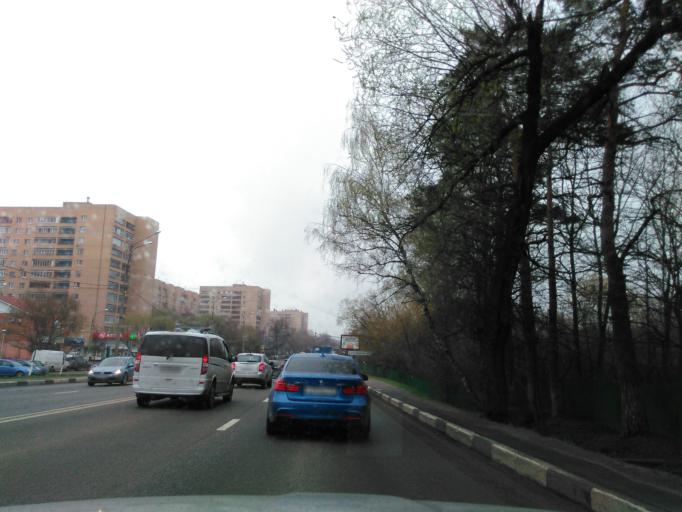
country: RU
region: Moskovskaya
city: Krasnogorsk
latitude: 55.8274
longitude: 37.3102
